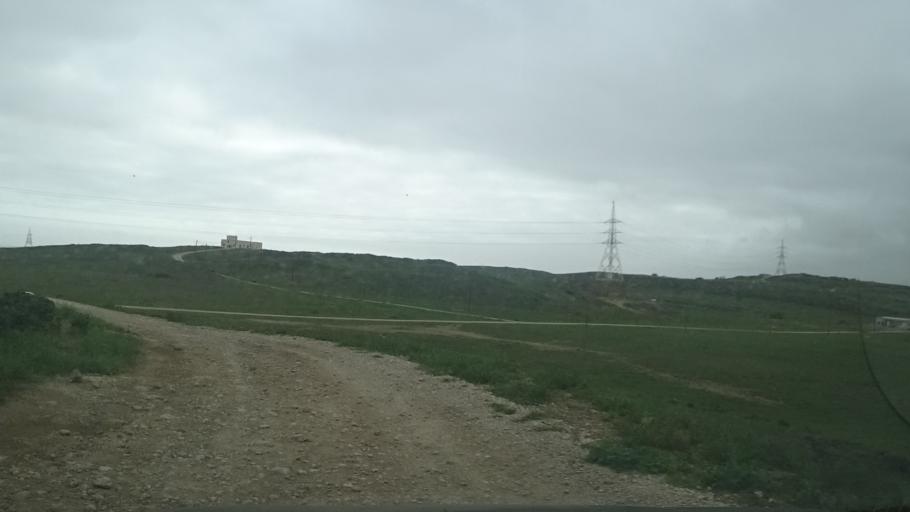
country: OM
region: Zufar
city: Salalah
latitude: 17.1129
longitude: 54.2372
